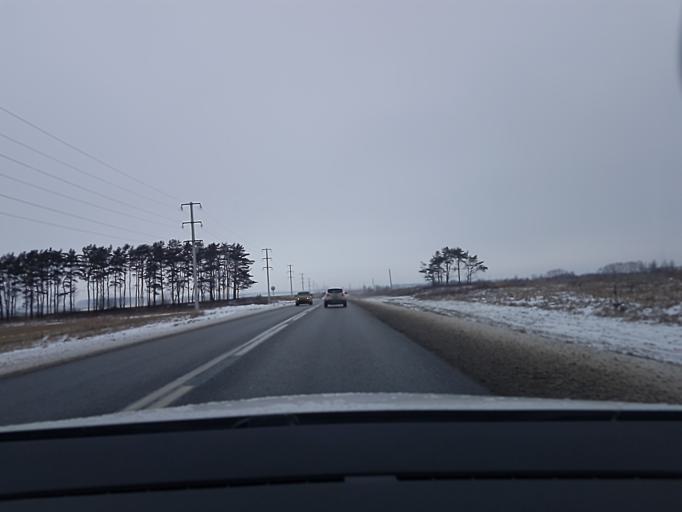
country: RU
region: Moskovskaya
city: Ozherel'ye
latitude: 54.7524
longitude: 38.2194
